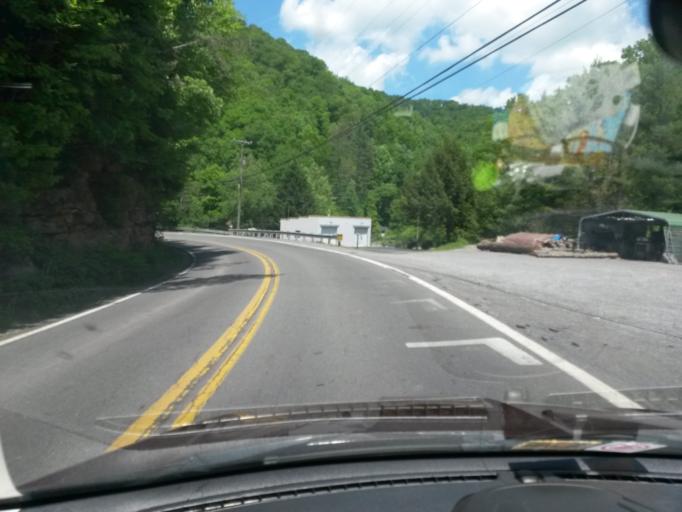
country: US
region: West Virginia
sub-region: Wyoming County
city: Pineville
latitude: 37.5048
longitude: -81.5411
